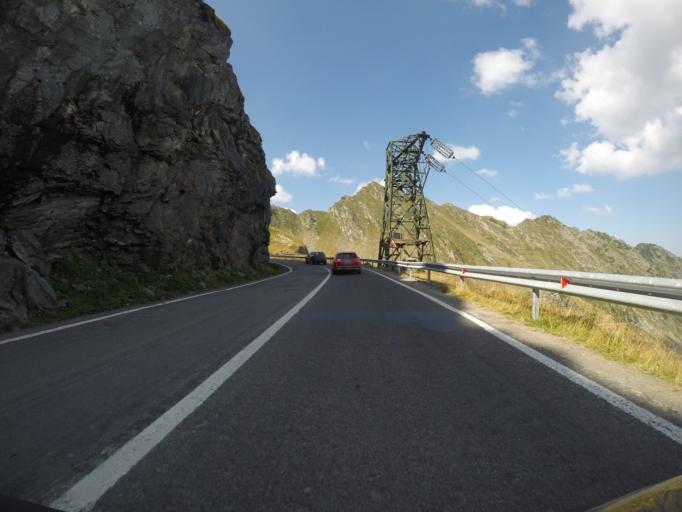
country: RO
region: Sibiu
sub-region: Comuna Cartisoara
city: Cartisoara
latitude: 45.6056
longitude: 24.6181
